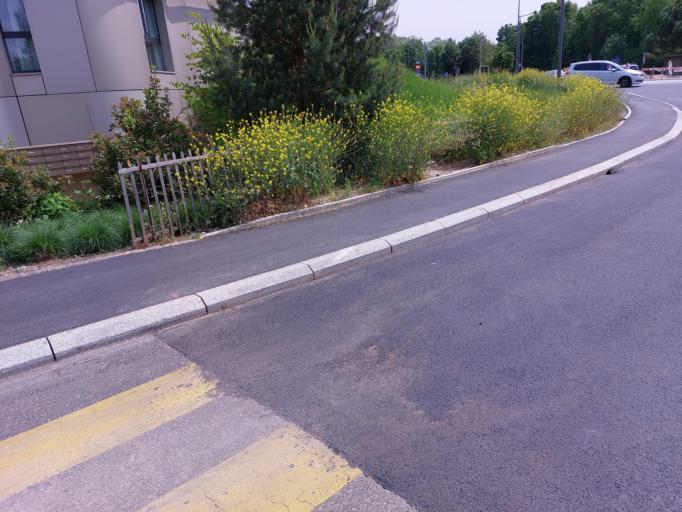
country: CH
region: Vaud
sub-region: Morges District
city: Preverenges
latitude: 46.5139
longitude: 6.5457
